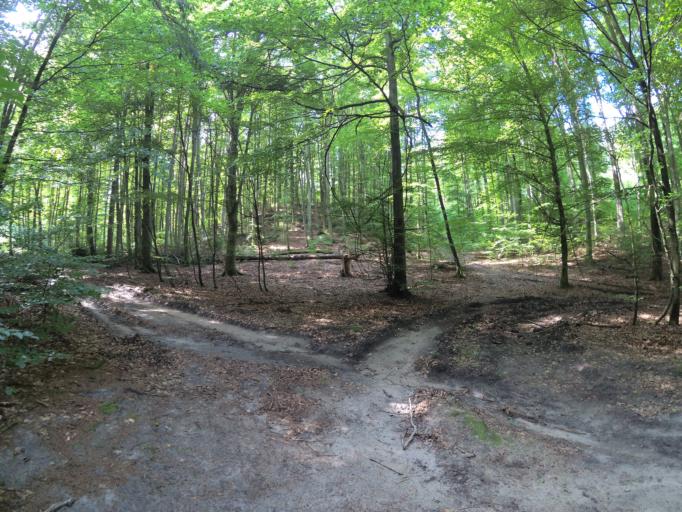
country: PL
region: Pomeranian Voivodeship
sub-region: Gdynia
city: Wielki Kack
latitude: 54.5075
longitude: 18.4539
